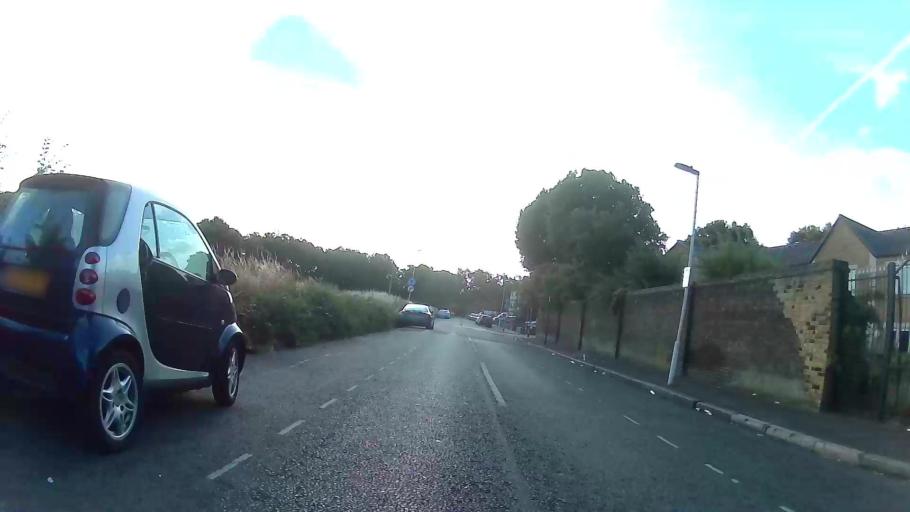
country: GB
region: England
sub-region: Greater London
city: East Ham
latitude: 51.5549
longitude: 0.0444
